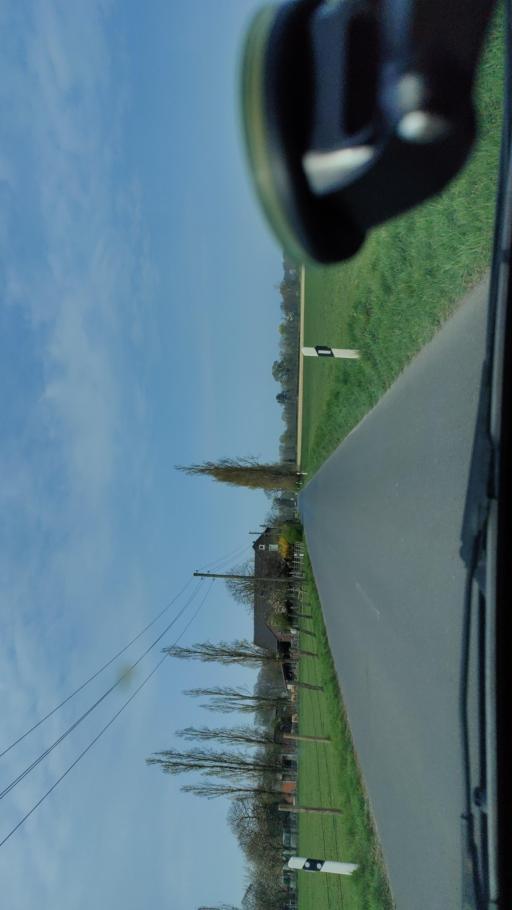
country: DE
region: North Rhine-Westphalia
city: Rheinberg
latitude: 51.5143
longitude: 6.6416
